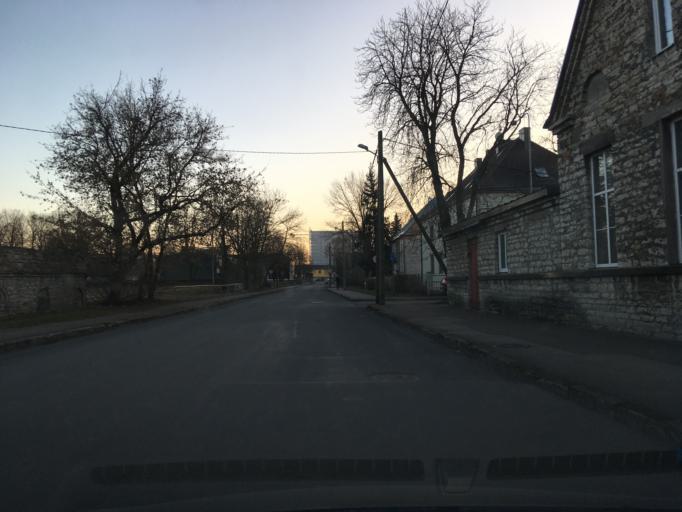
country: EE
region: Harju
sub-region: Tallinna linn
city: Tallinn
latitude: 59.4243
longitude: 24.7546
